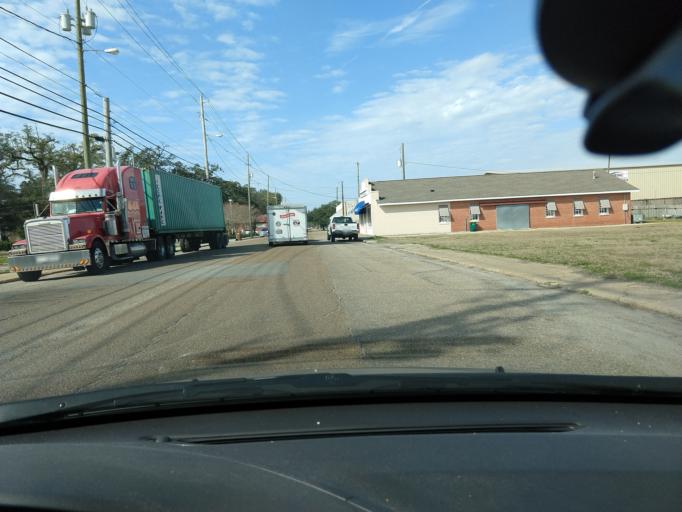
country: US
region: Mississippi
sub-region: Harrison County
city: Biloxi
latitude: 30.3956
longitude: -88.8681
